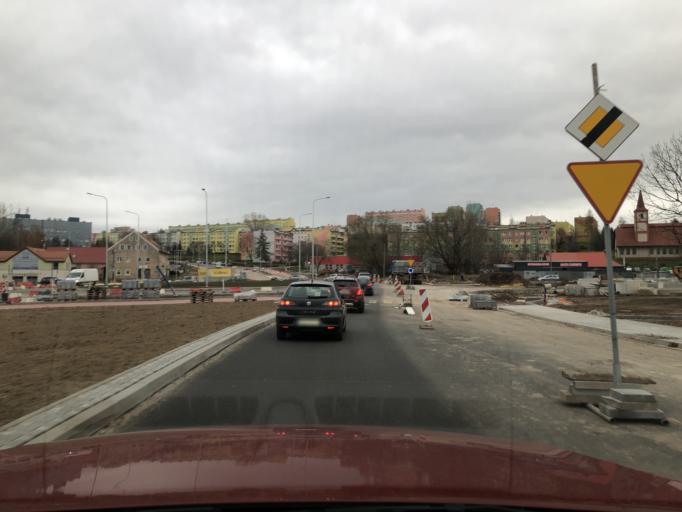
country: PL
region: Lower Silesian Voivodeship
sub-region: Powiat walbrzyski
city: Szczawno-Zdroj
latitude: 50.8147
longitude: 16.2735
